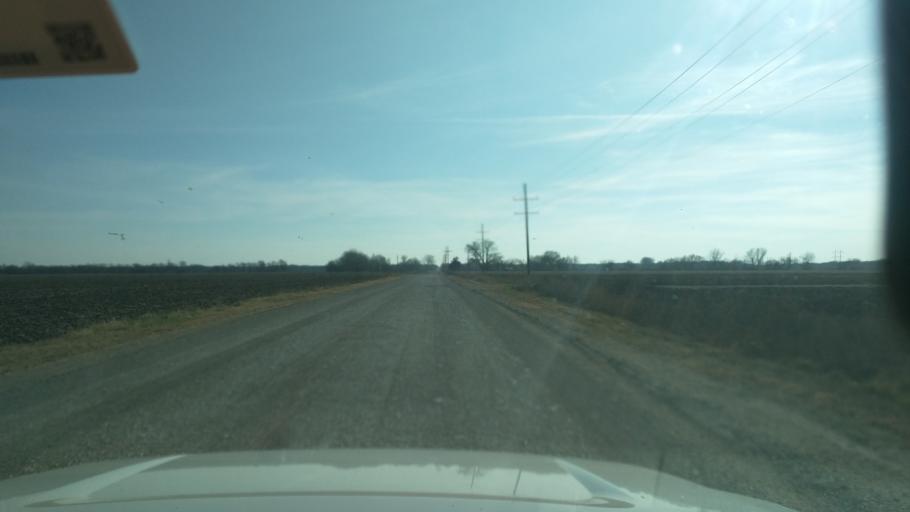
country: US
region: Kansas
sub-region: Lyon County
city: Emporia
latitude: 38.3784
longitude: -96.2080
